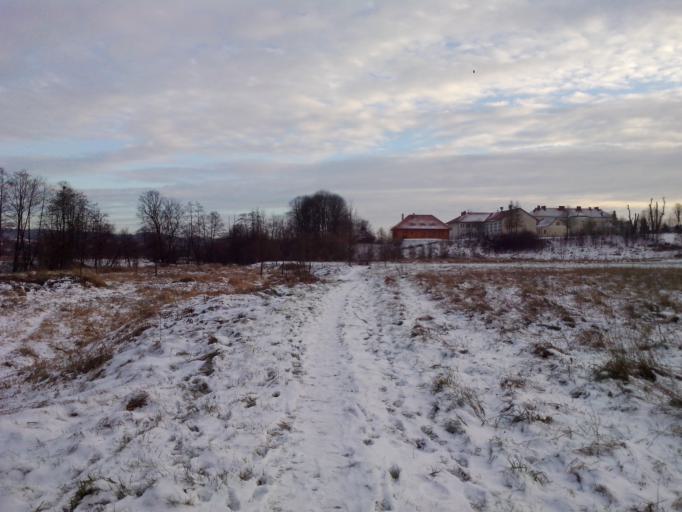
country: PL
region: Subcarpathian Voivodeship
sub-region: Powiat strzyzowski
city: Strzyzow
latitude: 49.8478
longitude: 21.8120
